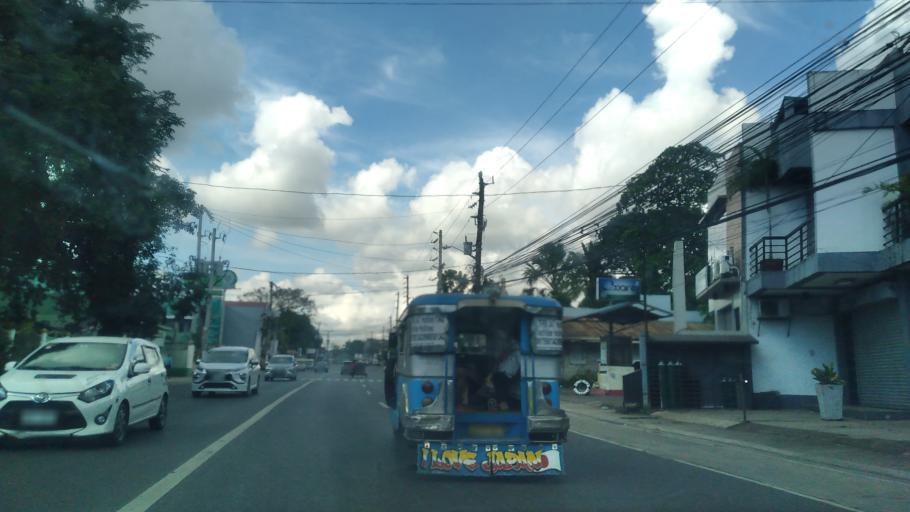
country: PH
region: Calabarzon
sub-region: Province of Quezon
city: Isabang
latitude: 13.9479
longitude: 121.5858
